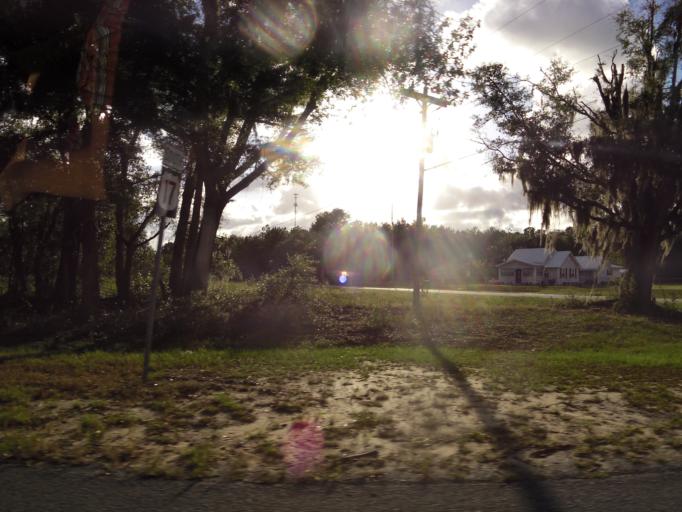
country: US
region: Georgia
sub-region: Liberty County
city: Midway
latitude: 31.7026
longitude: -81.4139
